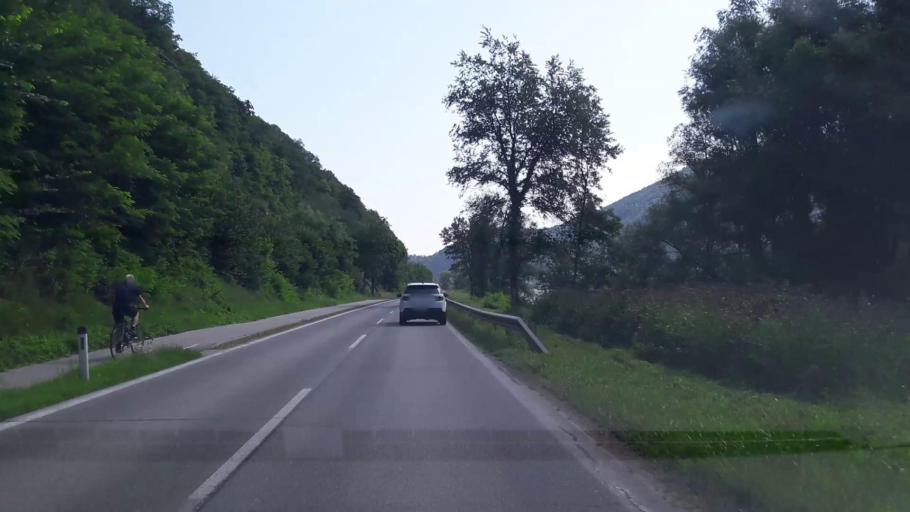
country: AT
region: Lower Austria
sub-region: Politischer Bezirk Krems
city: Aggsbach
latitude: 48.2757
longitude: 15.3840
